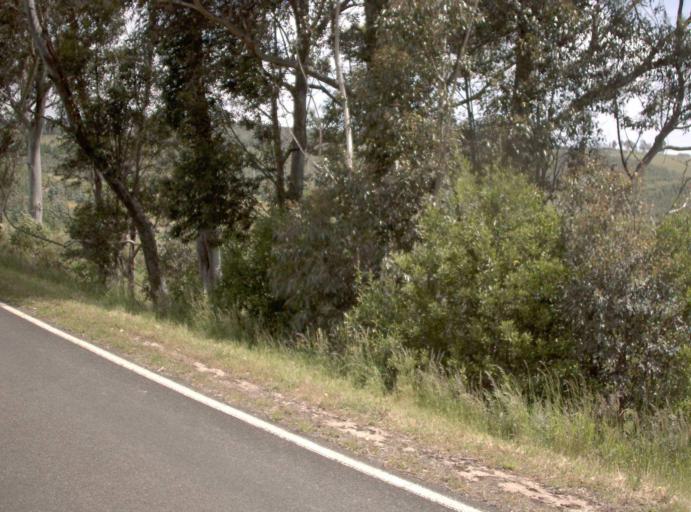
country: AU
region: Victoria
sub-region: Latrobe
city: Traralgon
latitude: -38.3524
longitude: 146.5681
